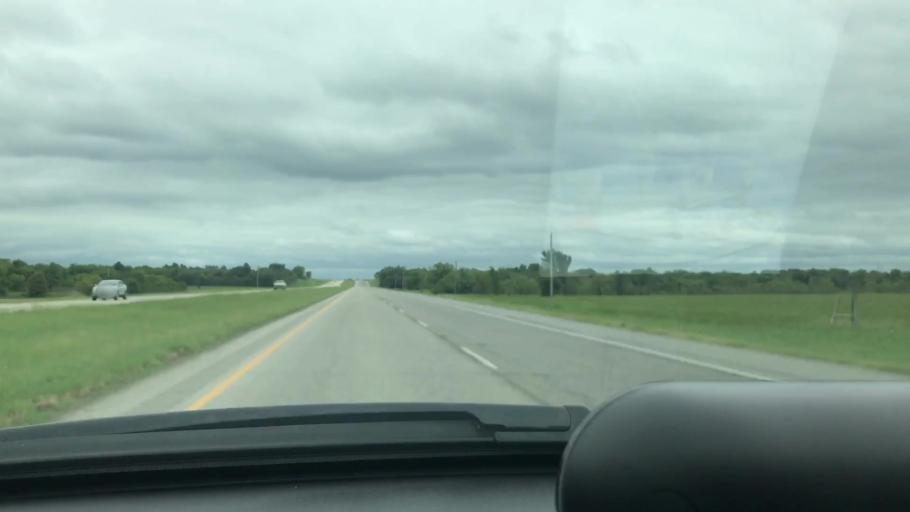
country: US
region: Oklahoma
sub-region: Wagoner County
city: Wagoner
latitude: 35.9843
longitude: -95.3773
